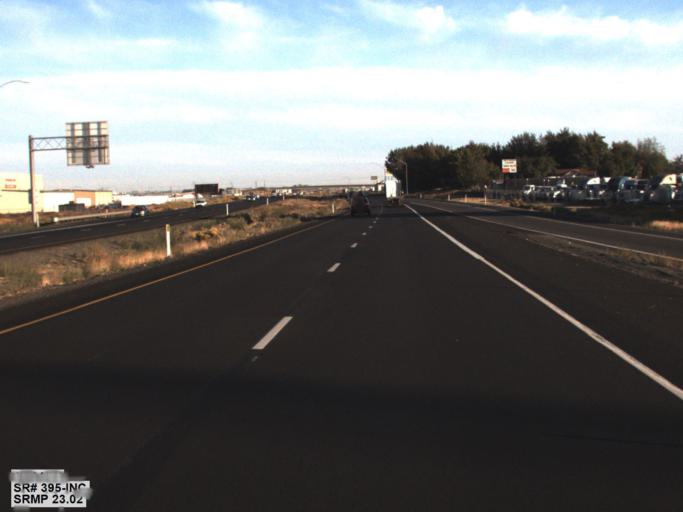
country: US
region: Washington
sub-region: Franklin County
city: Pasco
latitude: 46.2556
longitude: -119.0836
